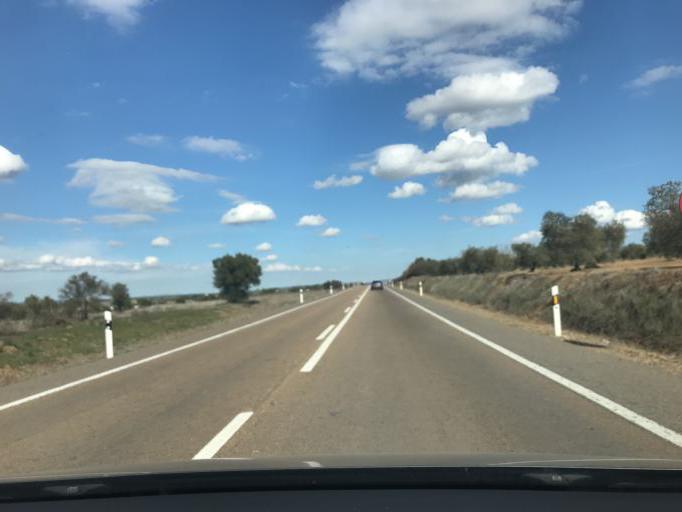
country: ES
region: Extremadura
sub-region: Provincia de Badajoz
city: Azuaga
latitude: 38.2648
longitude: -5.6935
